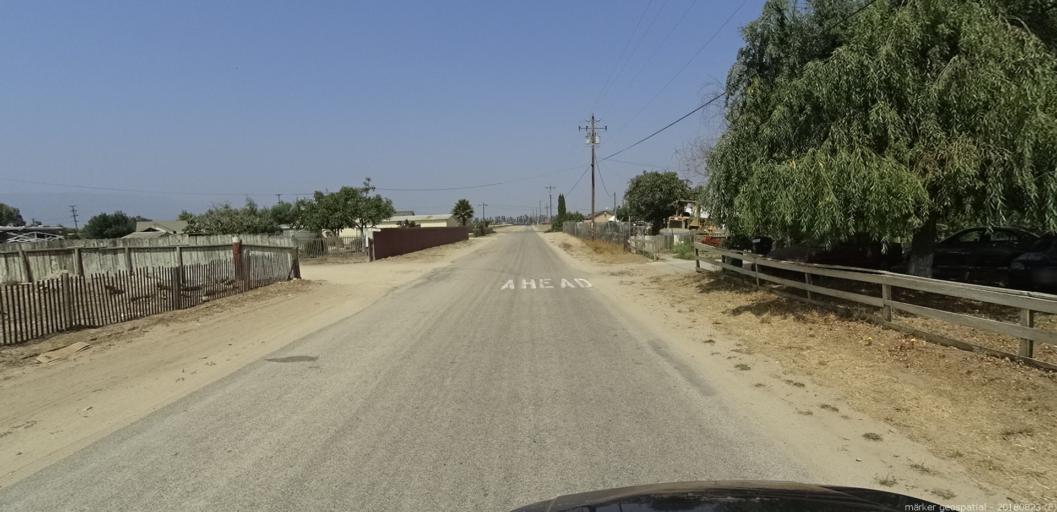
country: US
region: California
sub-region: Monterey County
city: Greenfield
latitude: 36.3277
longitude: -121.2601
